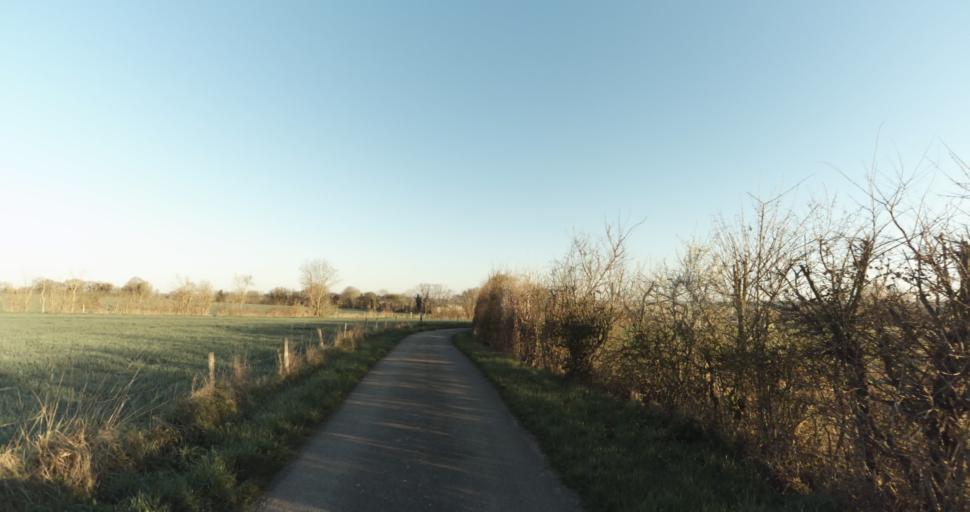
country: FR
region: Lower Normandy
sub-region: Departement du Calvados
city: Saint-Pierre-sur-Dives
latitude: 49.0254
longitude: -0.0168
